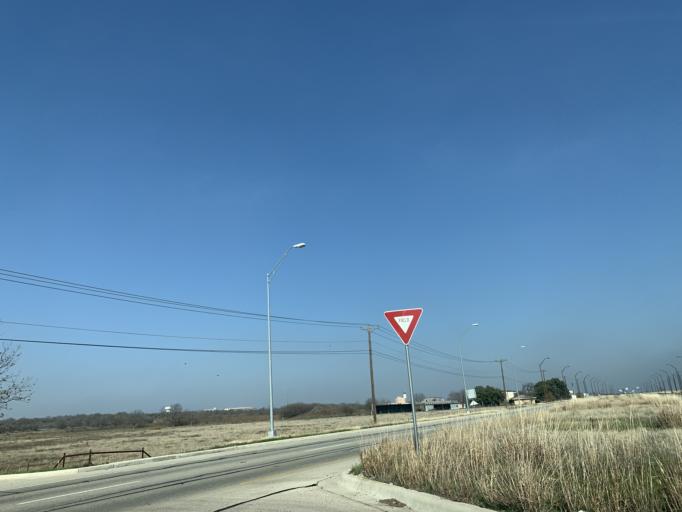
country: US
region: Texas
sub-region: Williamson County
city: Round Rock
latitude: 30.5468
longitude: -97.6484
